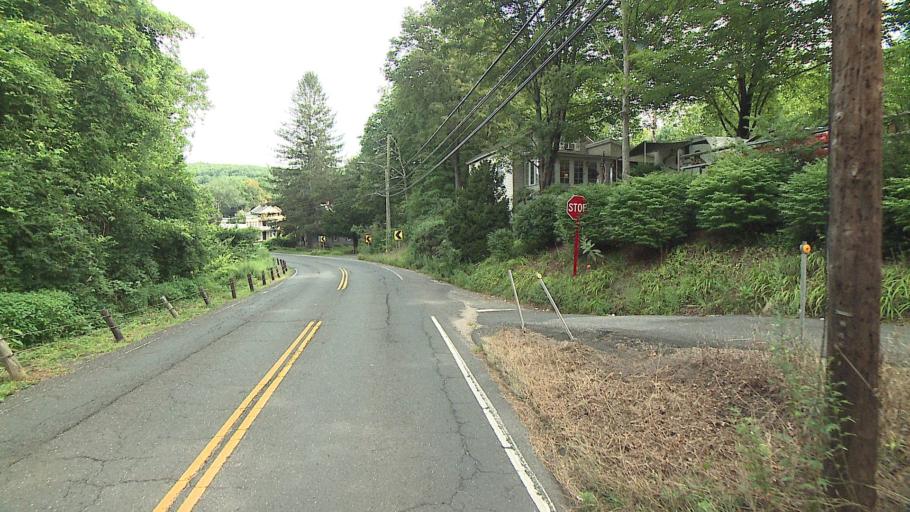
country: US
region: Connecticut
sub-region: Litchfield County
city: Woodbury
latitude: 41.5638
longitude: -73.2152
